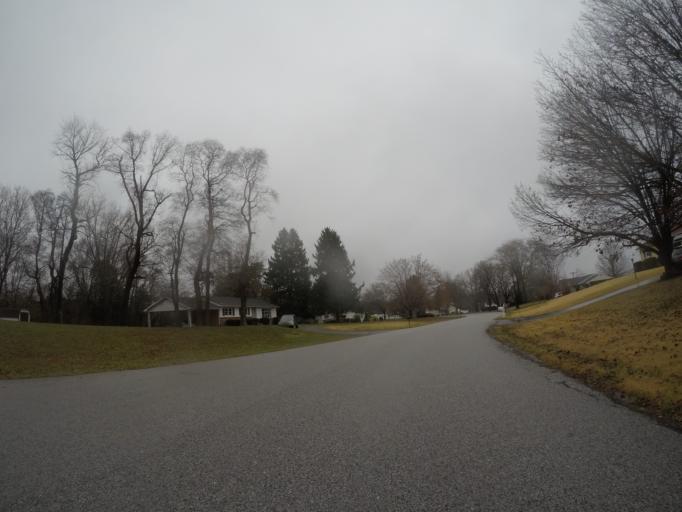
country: US
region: Maryland
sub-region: Howard County
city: Ellicott City
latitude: 39.2509
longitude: -76.8069
